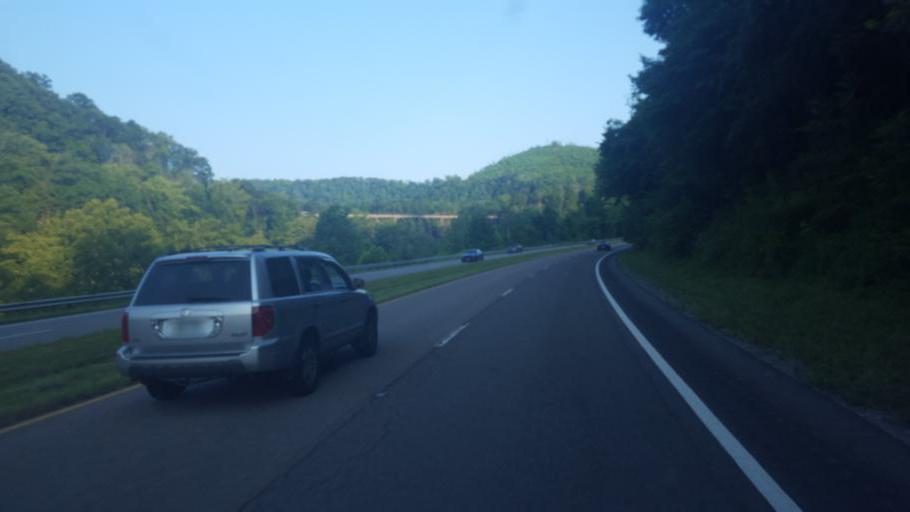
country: US
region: Tennessee
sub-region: Hawkins County
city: Church Hill
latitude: 36.6589
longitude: -82.7481
